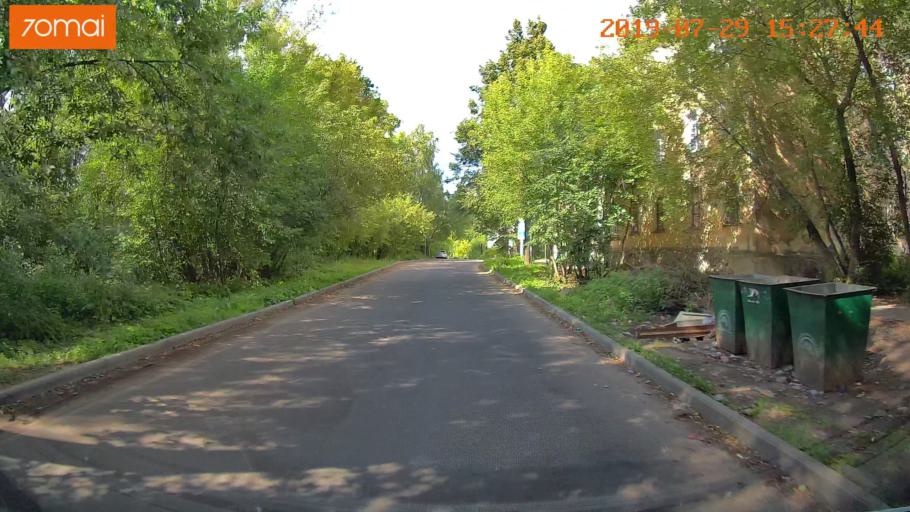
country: RU
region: Ivanovo
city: Bogorodskoye
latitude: 57.0245
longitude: 41.0104
